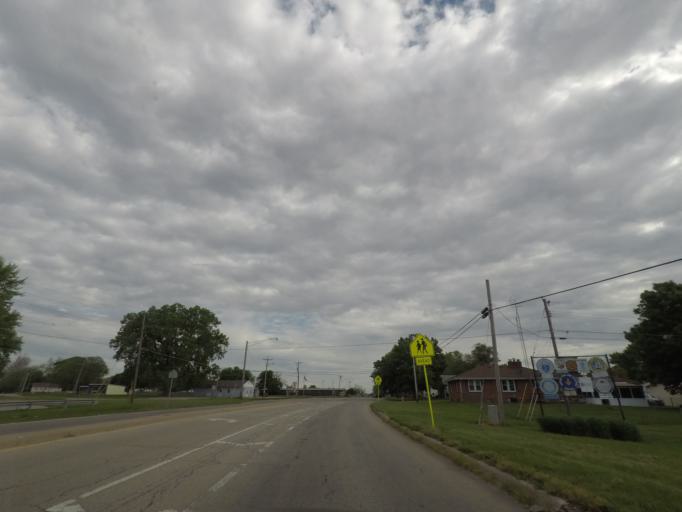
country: US
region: Illinois
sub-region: Logan County
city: Lincoln
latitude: 40.1374
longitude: -89.3488
